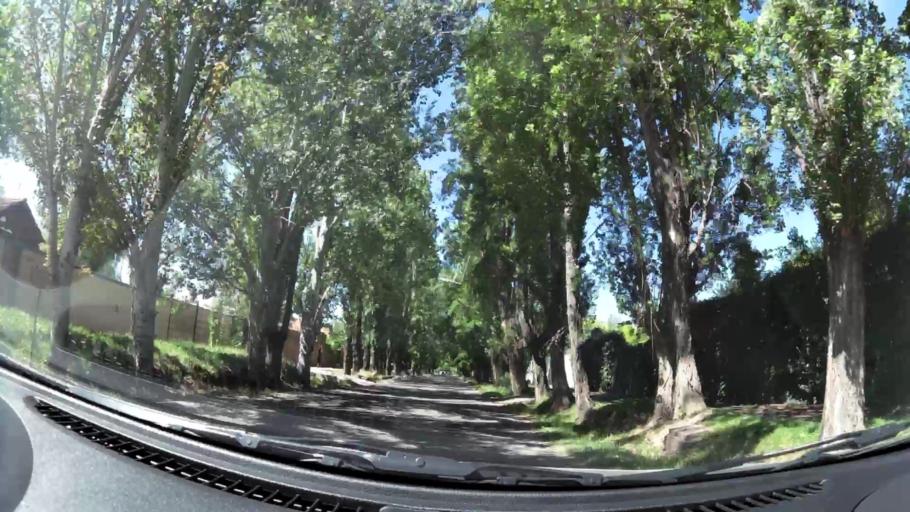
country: AR
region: Mendoza
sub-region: Departamento de Godoy Cruz
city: Godoy Cruz
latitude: -32.9643
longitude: -68.8638
